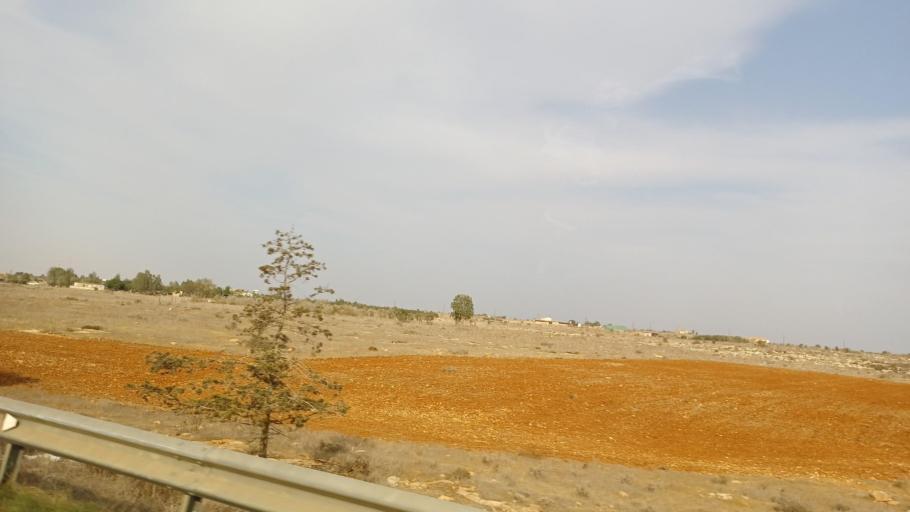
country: CY
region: Ammochostos
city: Frenaros
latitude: 35.0554
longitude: 33.9006
